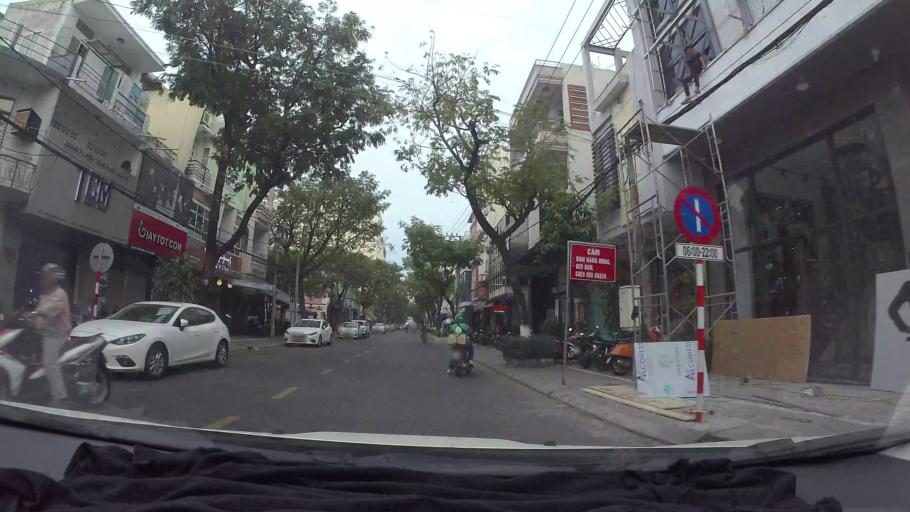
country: VN
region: Da Nang
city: Da Nang
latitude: 16.0651
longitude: 108.2208
